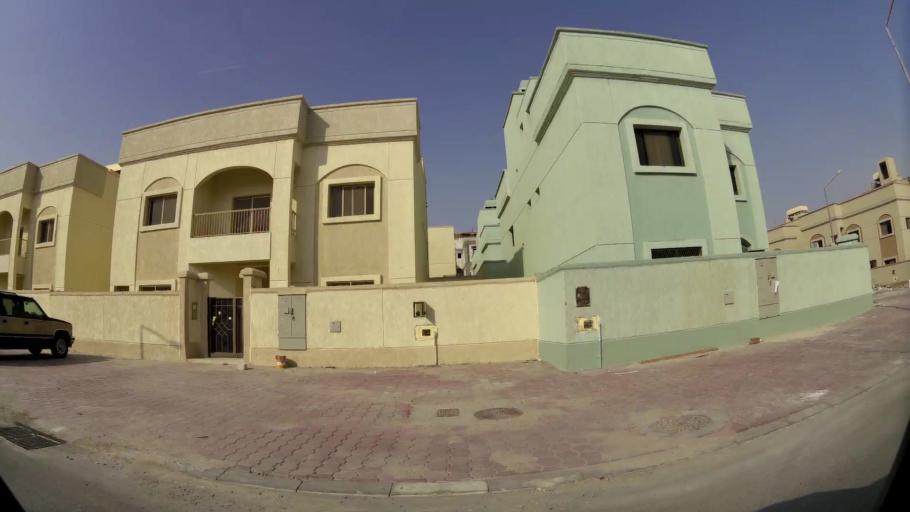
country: KW
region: Al Asimah
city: Ar Rabiyah
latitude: 29.3328
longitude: 47.8079
